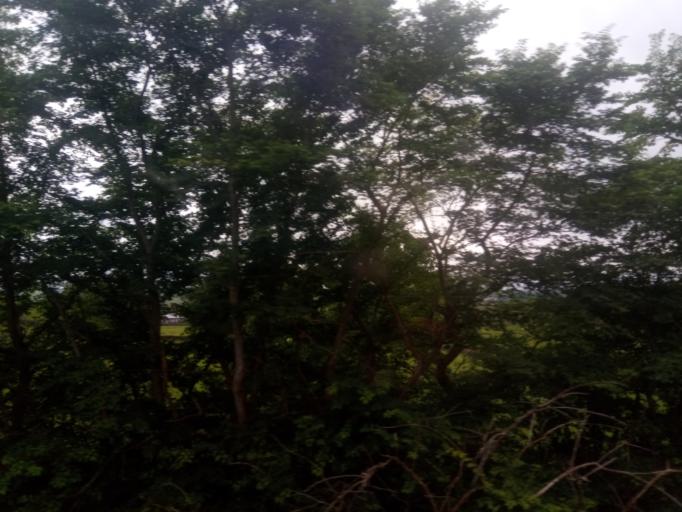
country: GB
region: England
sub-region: North Yorkshire
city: Settle
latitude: 54.0233
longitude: -2.2651
